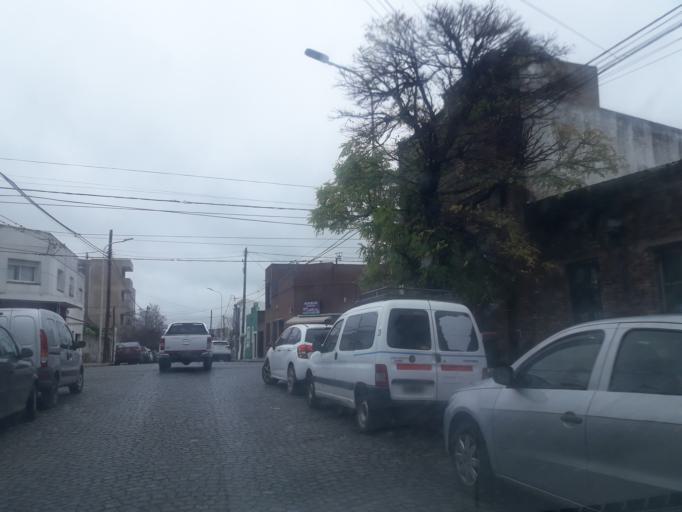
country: AR
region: Buenos Aires
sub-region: Partido de Tandil
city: Tandil
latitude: -37.3326
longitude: -59.1375
